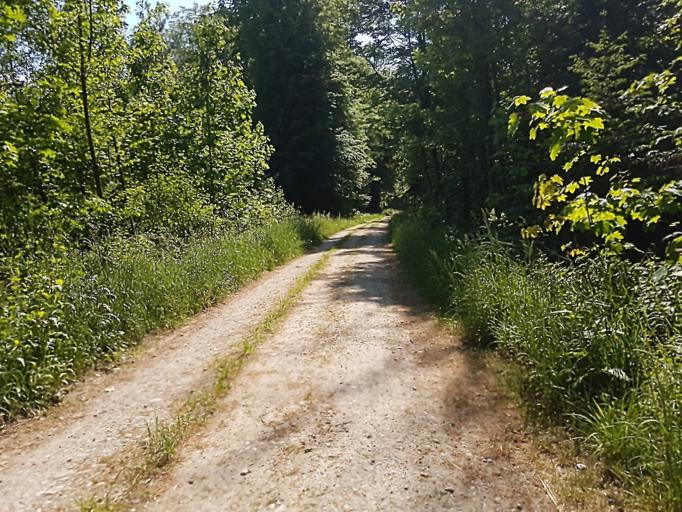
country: CH
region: Thurgau
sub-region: Arbon District
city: Amriswil
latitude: 47.5722
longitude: 9.3054
